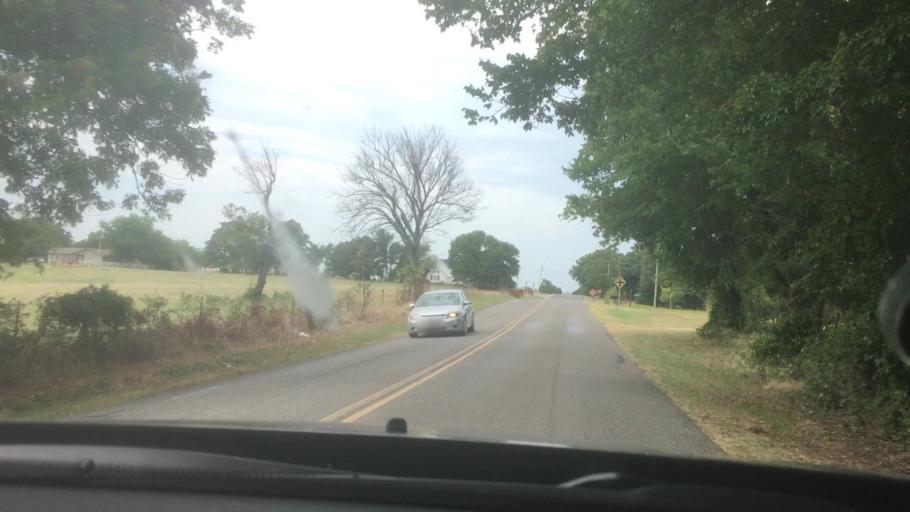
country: US
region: Oklahoma
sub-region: Murray County
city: Davis
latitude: 34.4899
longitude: -97.0555
